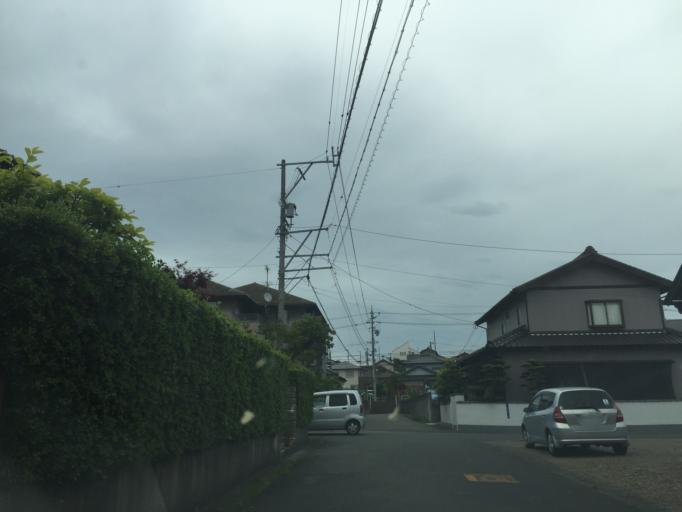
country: JP
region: Shizuoka
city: Kakegawa
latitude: 34.7805
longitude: 138.0190
